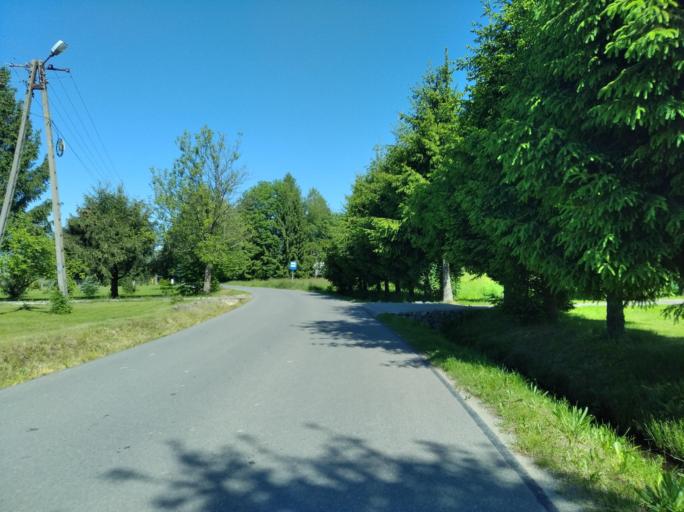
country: PL
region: Subcarpathian Voivodeship
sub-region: Powiat krosnienski
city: Korczyna
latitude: 49.7210
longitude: 21.7888
